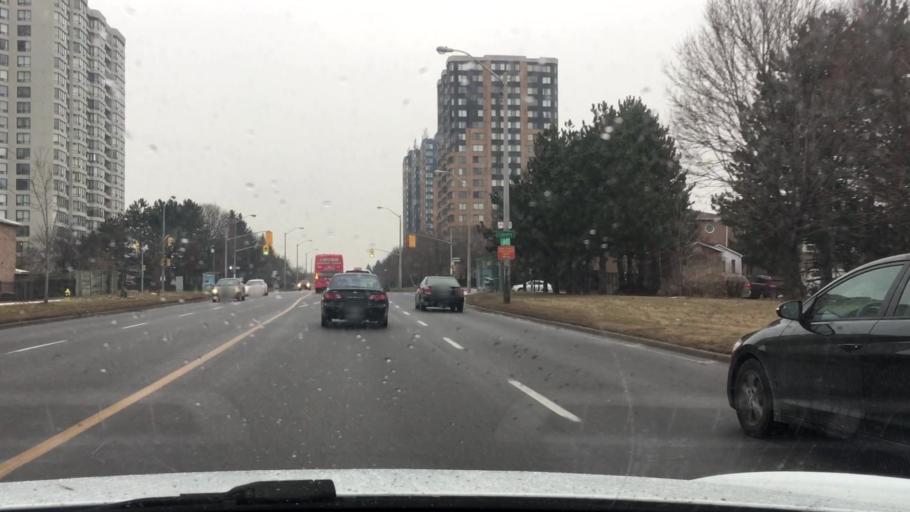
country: CA
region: Ontario
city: Markham
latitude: 43.8217
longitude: -79.2736
